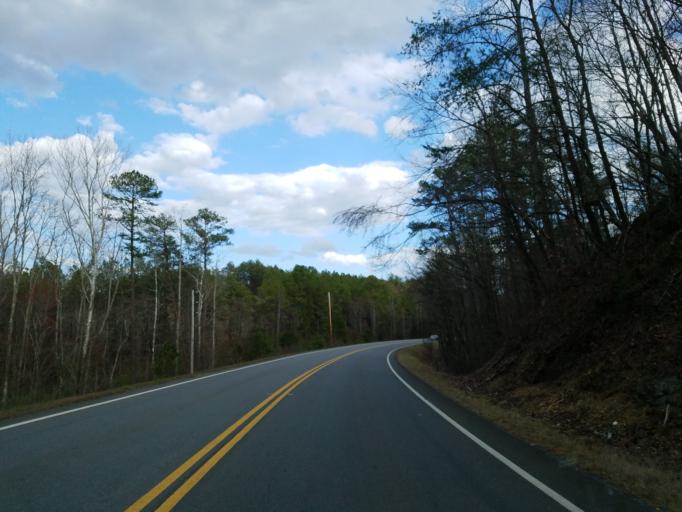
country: US
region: Georgia
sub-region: Bartow County
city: Rydal
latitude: 34.4517
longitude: -84.7592
